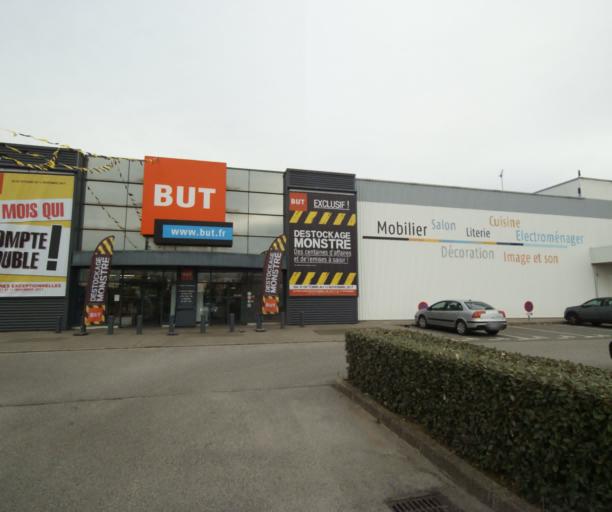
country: FR
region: Centre
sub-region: Departement d'Eure-et-Loir
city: Dreux
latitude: 48.7496
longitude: 1.3475
